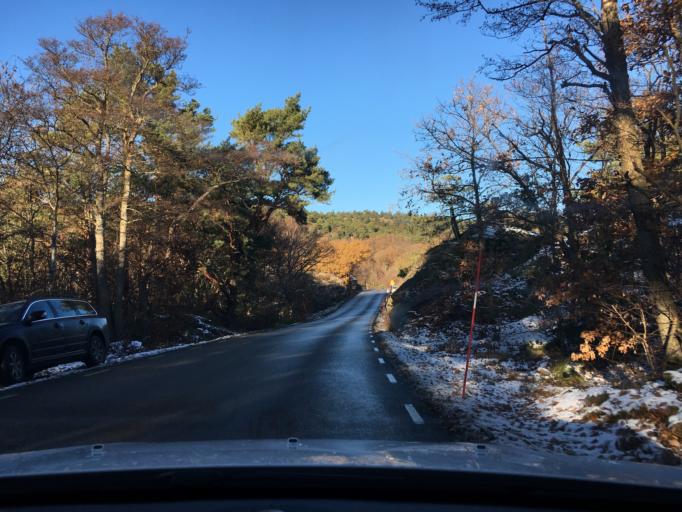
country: SE
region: Vaestra Goetaland
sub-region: Tjorns Kommun
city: Myggenas
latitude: 58.0633
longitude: 11.6819
